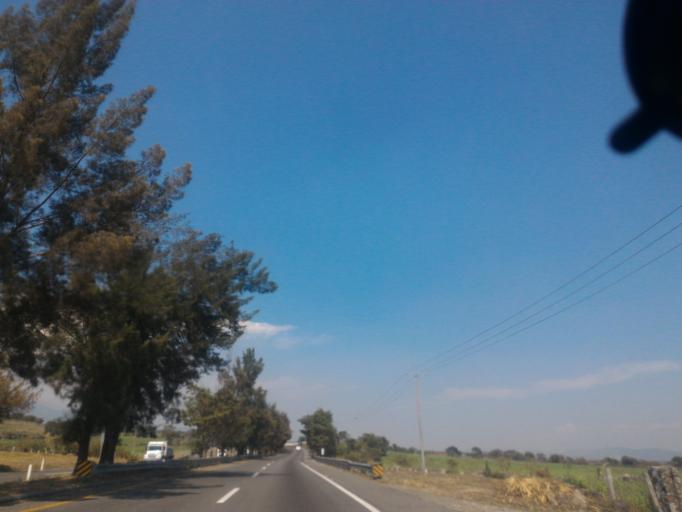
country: MX
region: Colima
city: Queseria
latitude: 19.3720
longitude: -103.5604
